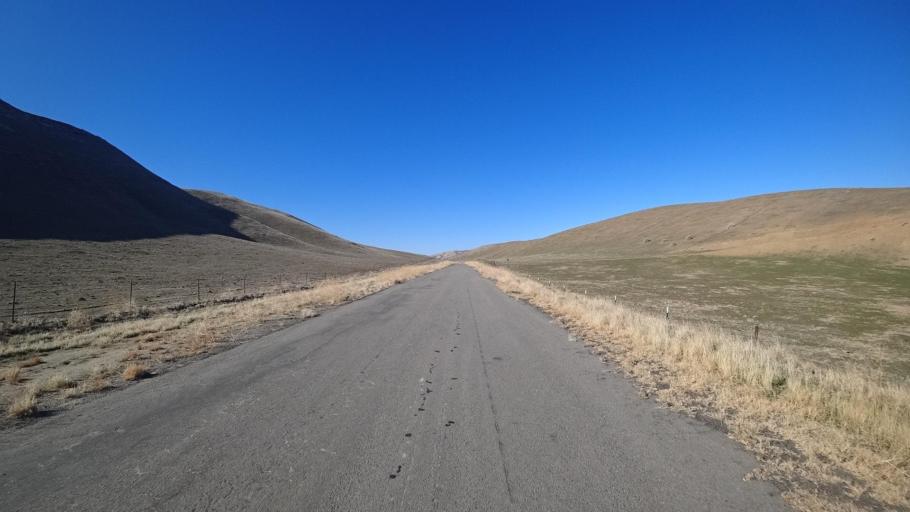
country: US
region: California
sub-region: Kern County
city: Maricopa
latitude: 34.9786
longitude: -119.4651
